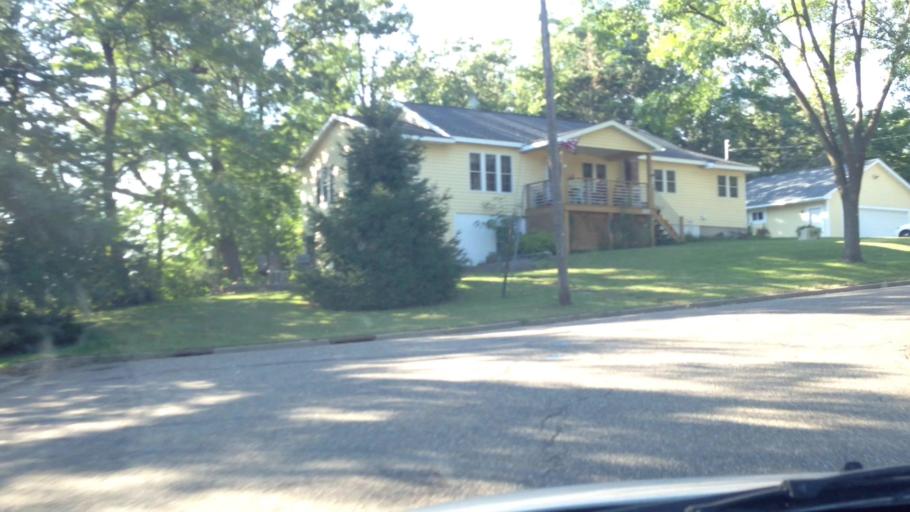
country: US
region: Wisconsin
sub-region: Saint Croix County
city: North Hudson
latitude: 44.9892
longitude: -92.7560
